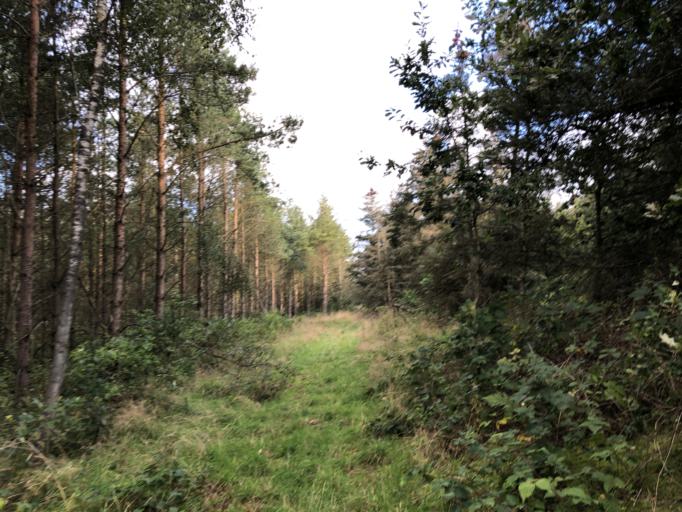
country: DK
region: Central Jutland
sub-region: Holstebro Kommune
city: Ulfborg
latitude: 56.3731
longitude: 8.3432
